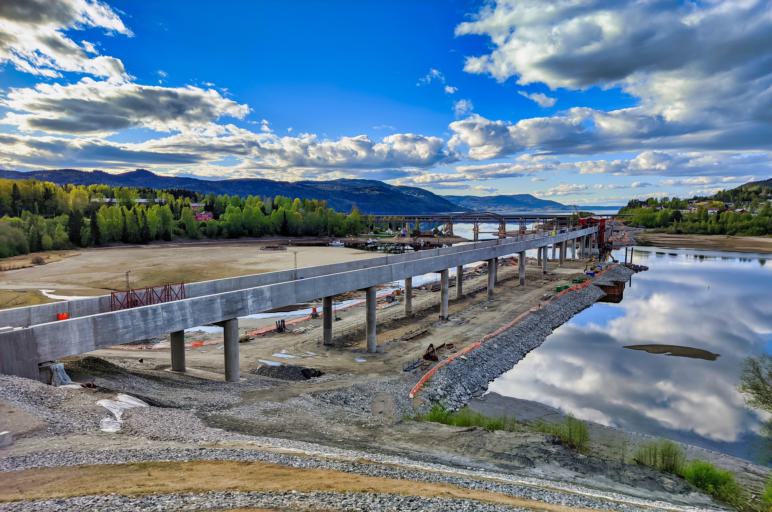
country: NO
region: Akershus
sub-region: Eidsvoll
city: Eidsvoll
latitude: 60.3910
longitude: 11.2391
